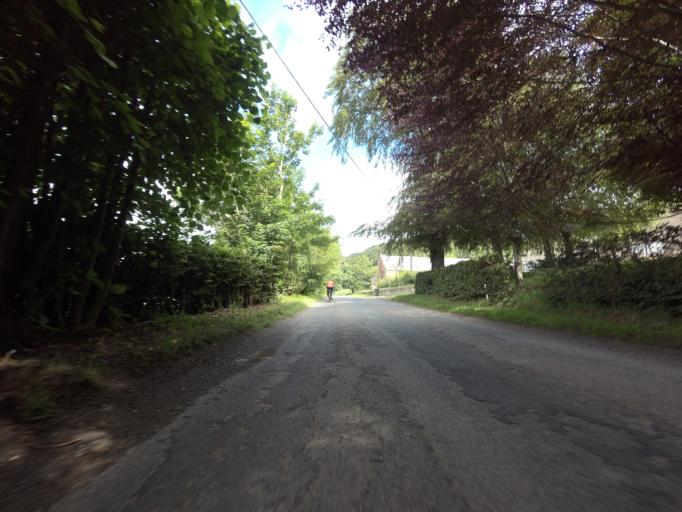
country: GB
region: Scotland
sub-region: Aberdeenshire
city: Turriff
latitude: 57.5479
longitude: -2.4824
